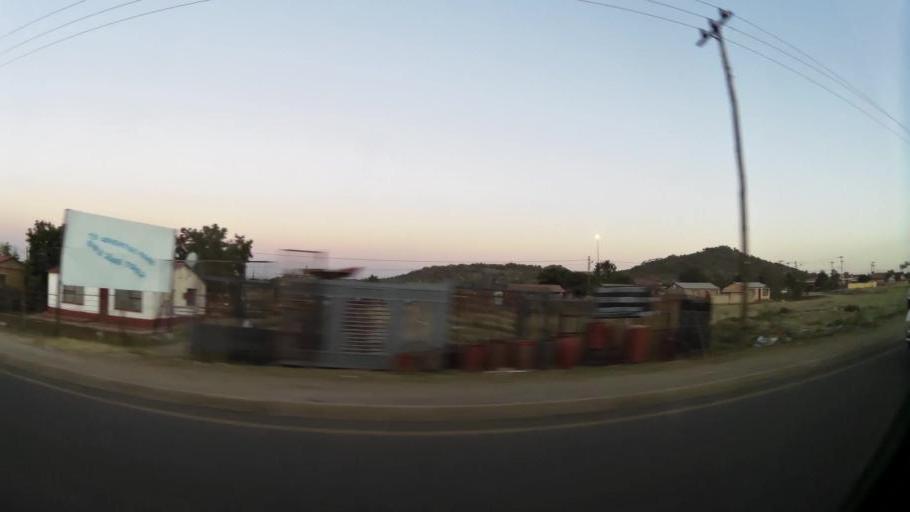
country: ZA
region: North-West
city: Ga-Rankuwa
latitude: -25.5996
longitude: 27.9747
